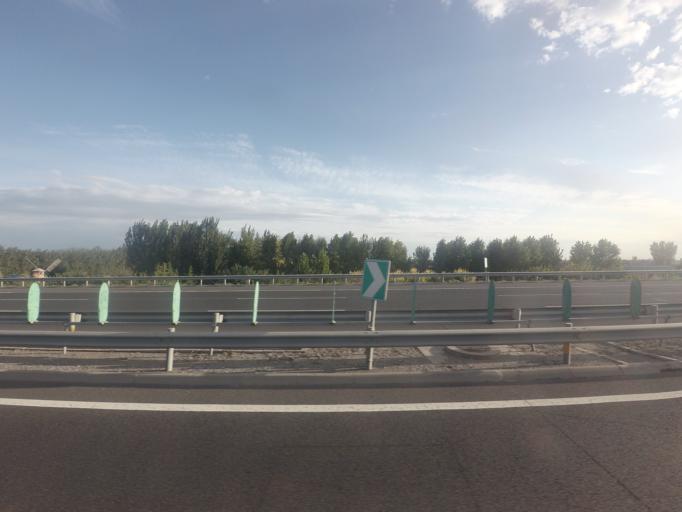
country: CN
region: Beijing
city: Yangsong
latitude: 40.2680
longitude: 116.6781
